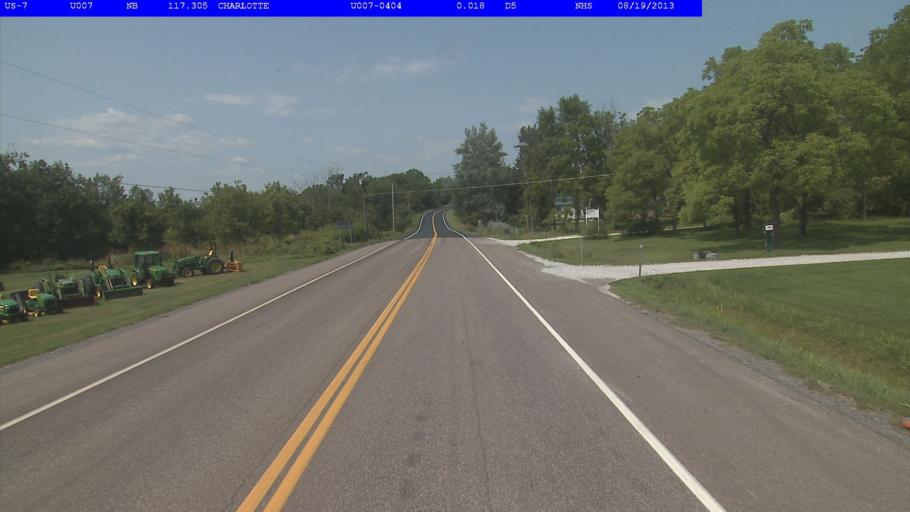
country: US
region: Vermont
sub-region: Addison County
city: Vergennes
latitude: 44.2628
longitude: -73.2304
